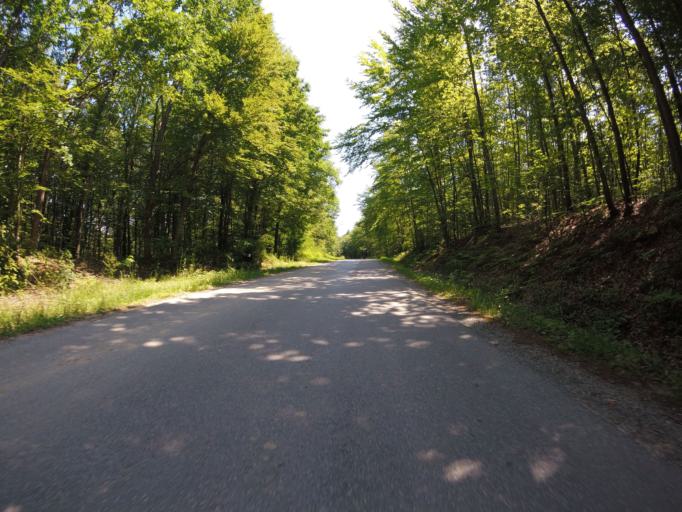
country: HR
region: Grad Zagreb
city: Strmec
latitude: 45.5866
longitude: 15.9590
